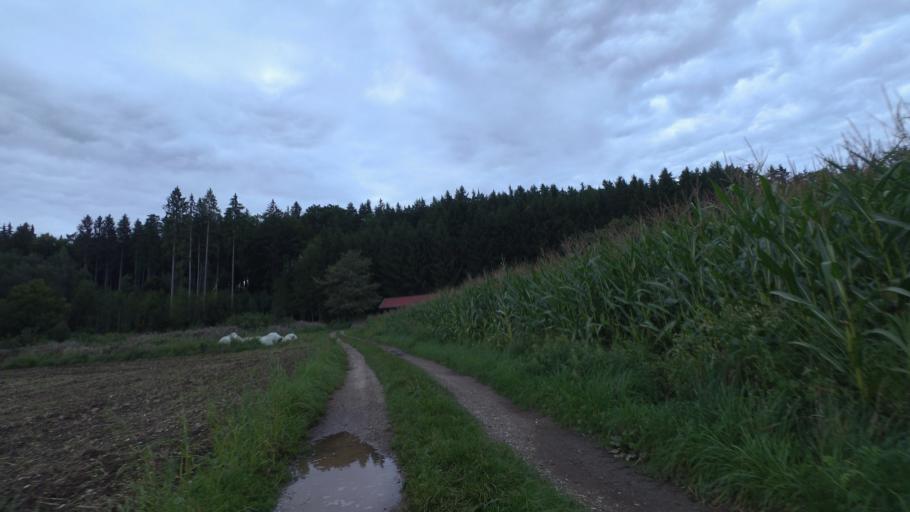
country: DE
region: Bavaria
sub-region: Upper Bavaria
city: Nussdorf
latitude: 47.8907
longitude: 12.5769
